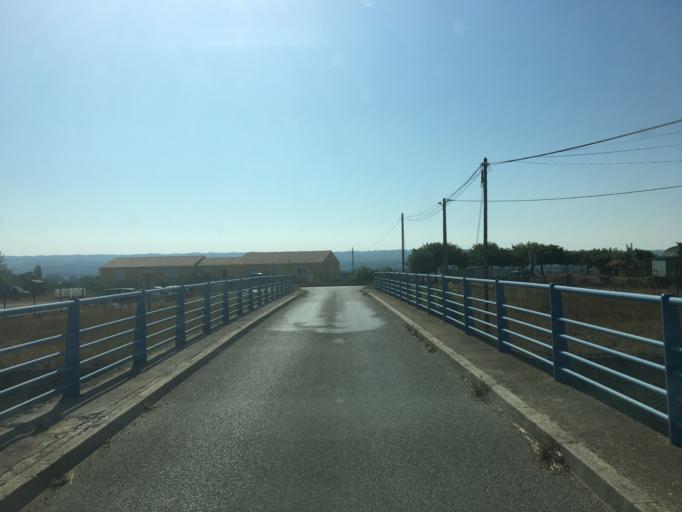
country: FR
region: Provence-Alpes-Cote d'Azur
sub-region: Departement des Alpes-de-Haute-Provence
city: Sainte-Tulle
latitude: 43.7989
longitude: 5.7831
